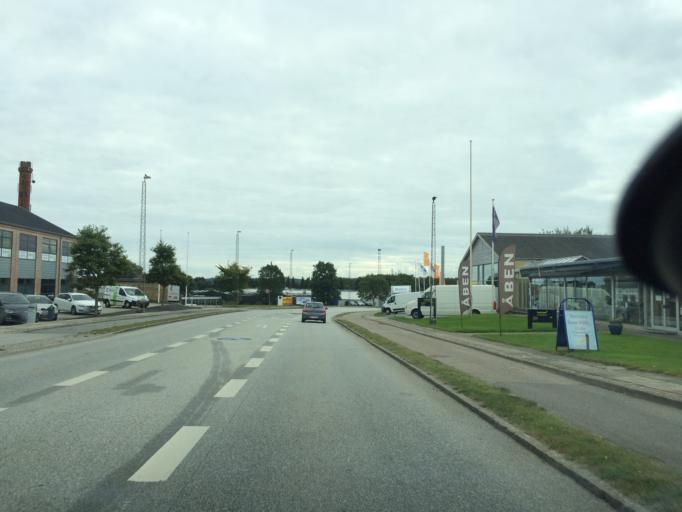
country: DK
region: South Denmark
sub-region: Aabenraa Kommune
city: Aabenraa
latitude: 55.0510
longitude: 9.4034
